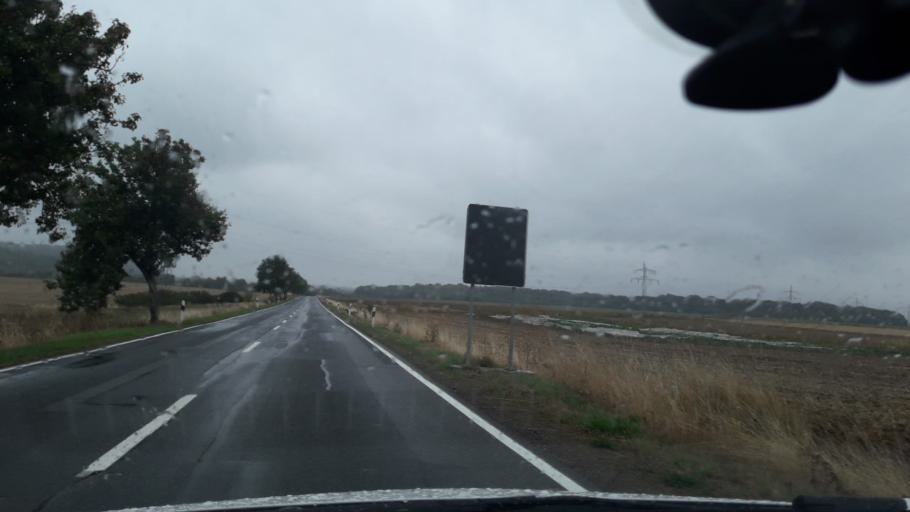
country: DE
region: Lower Saxony
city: Gielde
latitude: 51.9700
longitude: 10.4943
